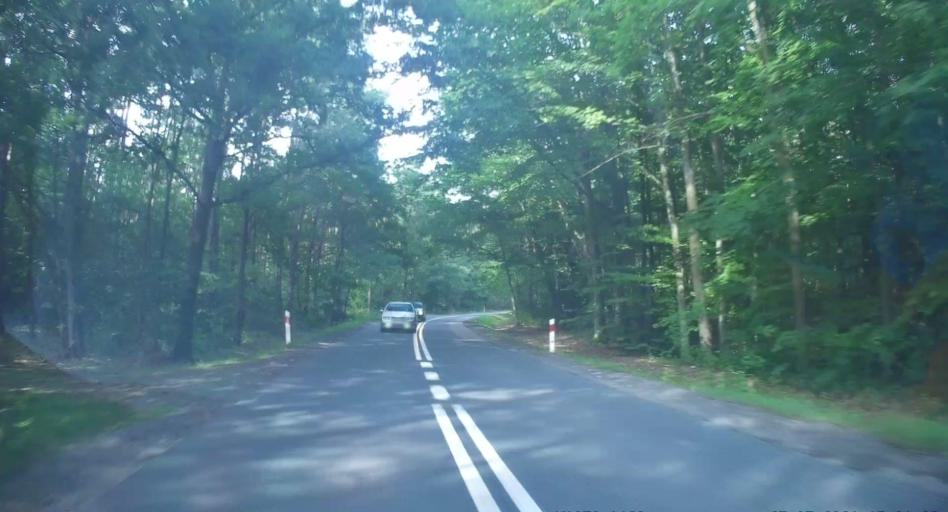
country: PL
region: Lodz Voivodeship
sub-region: Powiat tomaszowski
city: Rzeczyca
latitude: 51.5725
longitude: 20.2773
